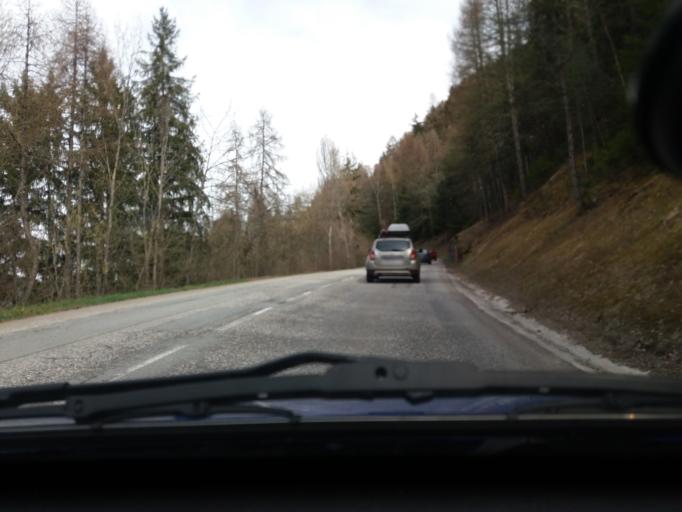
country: FR
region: Rhone-Alpes
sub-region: Departement de la Savoie
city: Macot-la-Plagne
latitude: 45.5489
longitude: 6.6703
